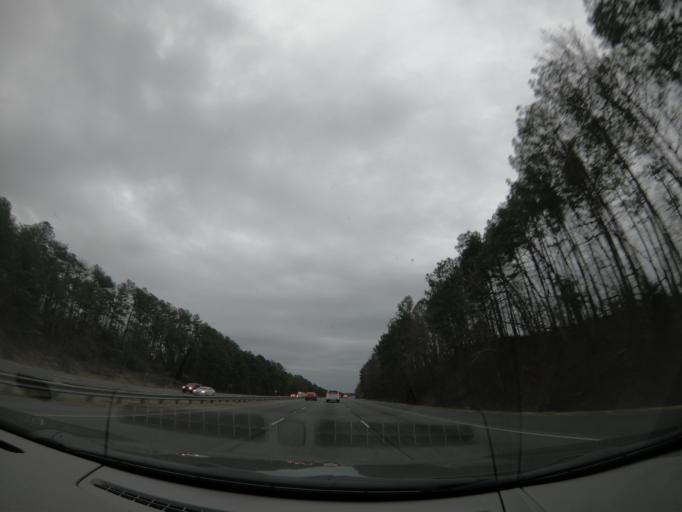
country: US
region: Georgia
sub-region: Gordon County
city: Calhoun
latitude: 34.6184
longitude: -84.9659
